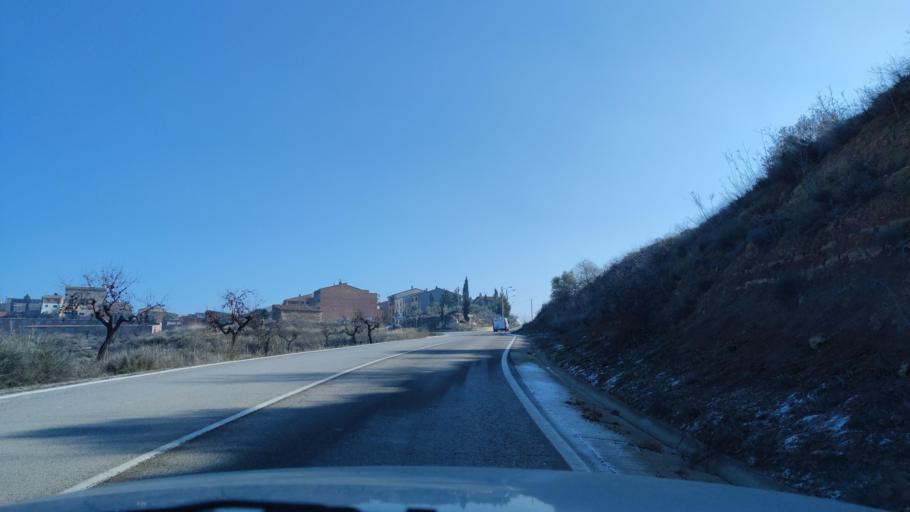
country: ES
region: Catalonia
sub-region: Provincia de Lleida
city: Torrebesses
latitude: 41.4263
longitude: 0.5896
